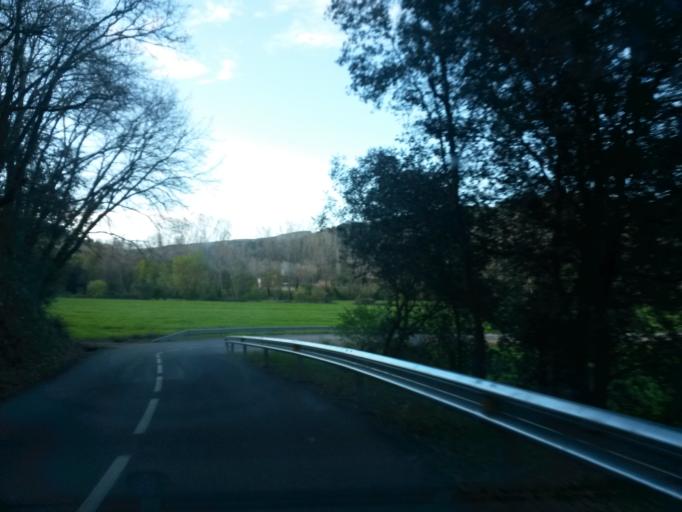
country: ES
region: Catalonia
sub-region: Provincia de Girona
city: Angles
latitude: 41.9775
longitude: 2.6725
